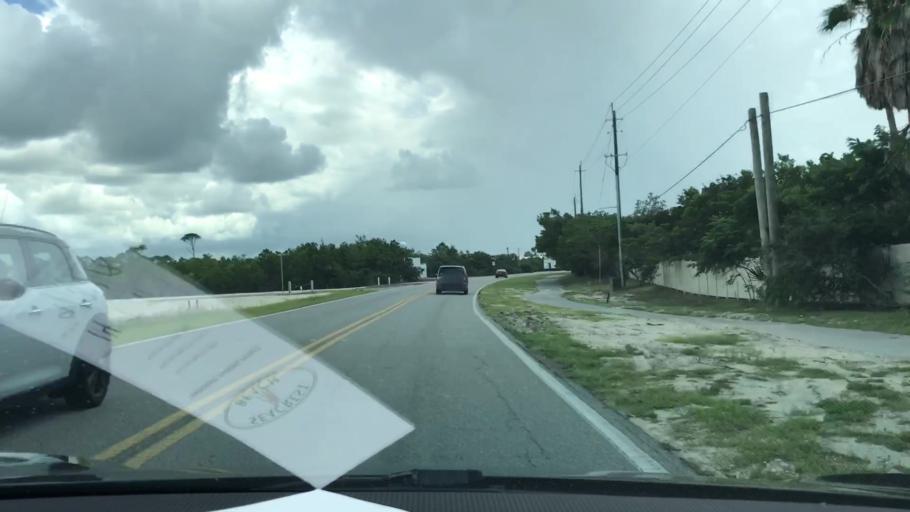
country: US
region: Florida
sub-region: Walton County
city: Seaside
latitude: 30.2870
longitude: -86.0362
